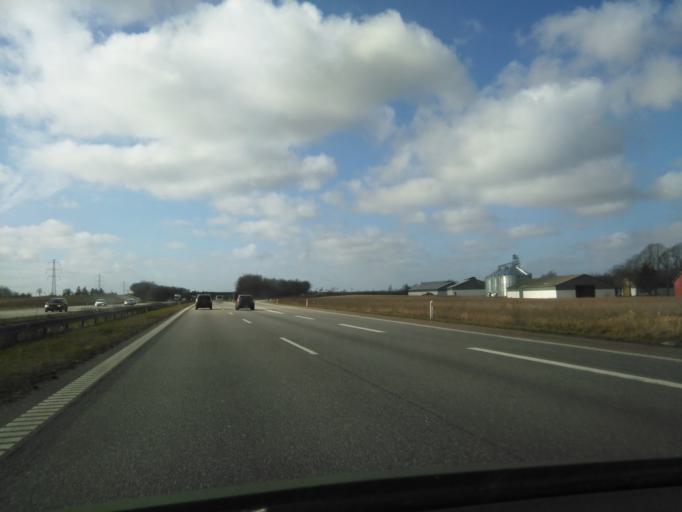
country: DK
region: Zealand
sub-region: Koge Kommune
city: Borup
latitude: 55.4579
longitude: 11.9902
